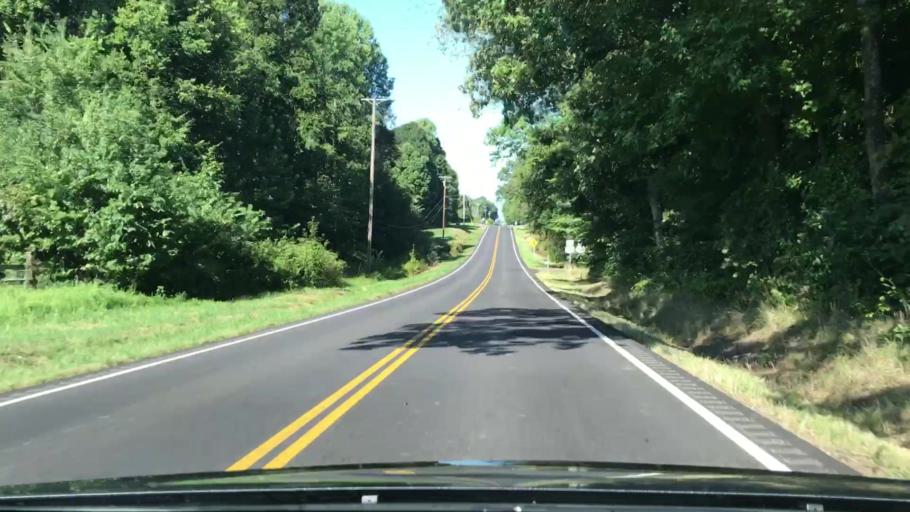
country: US
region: Kentucky
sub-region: Marshall County
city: Benton
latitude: 36.7651
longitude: -88.3906
